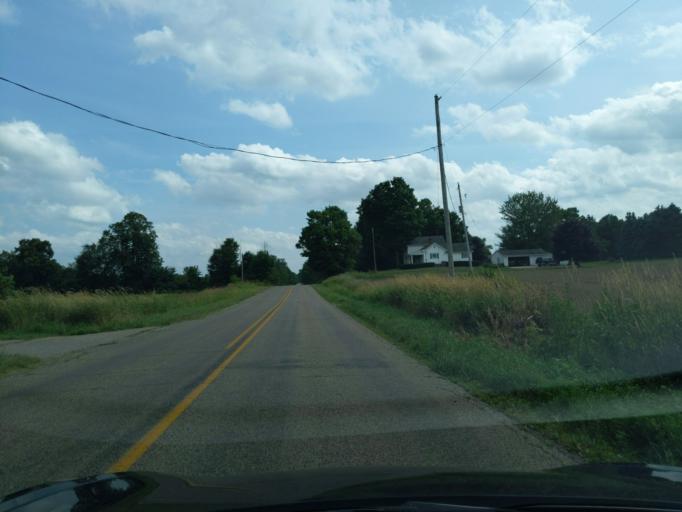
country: US
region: Michigan
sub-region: Eaton County
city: Eaton Rapids
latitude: 42.5437
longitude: -84.6018
